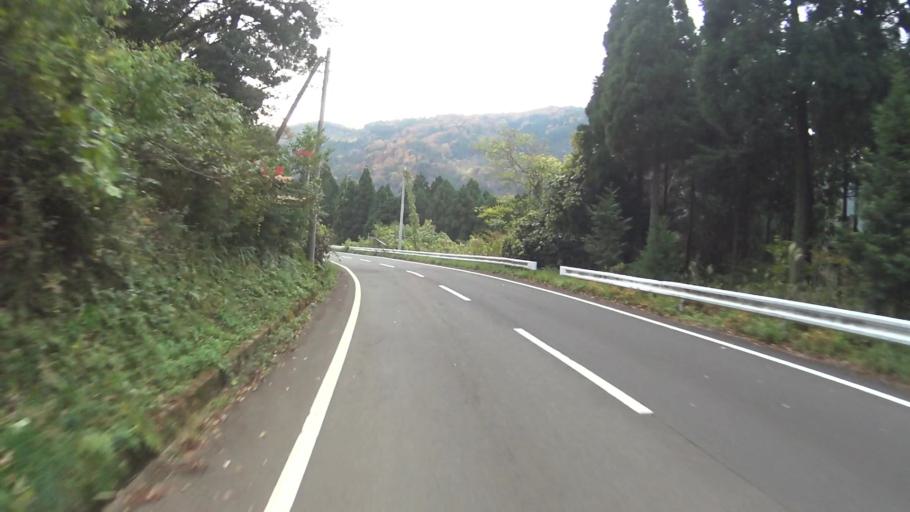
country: JP
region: Kyoto
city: Maizuru
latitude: 35.5652
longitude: 135.4581
